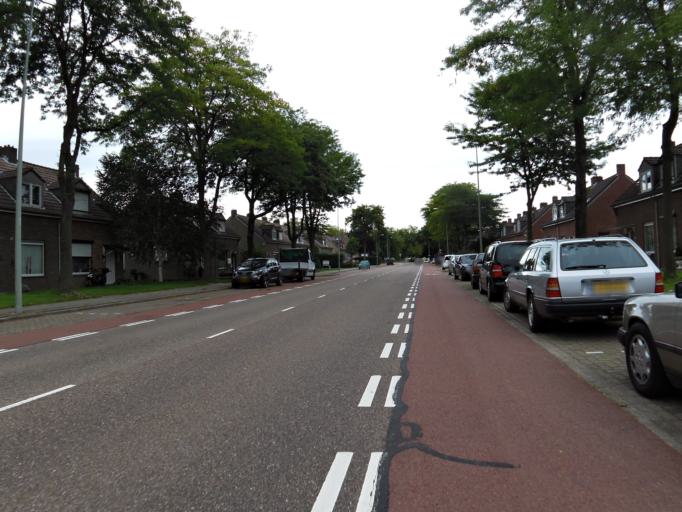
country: NL
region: Limburg
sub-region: Gemeente Heerlen
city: Heerlen
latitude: 50.8815
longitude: 6.0024
